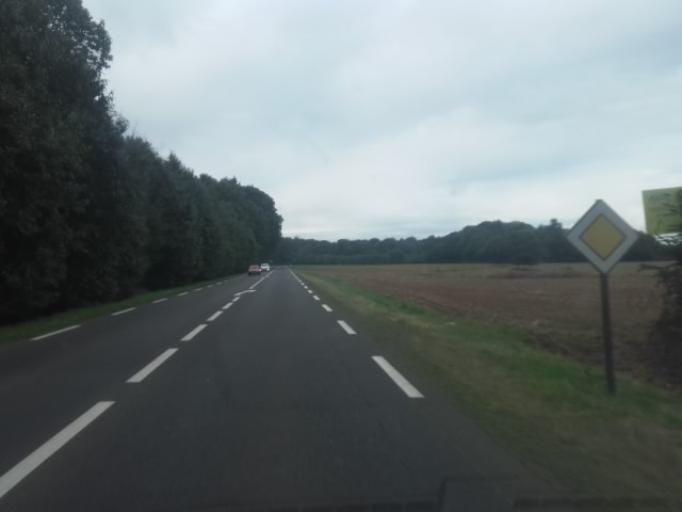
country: FR
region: Brittany
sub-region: Departement des Cotes-d'Armor
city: Plelo
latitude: 48.5869
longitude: -2.9380
